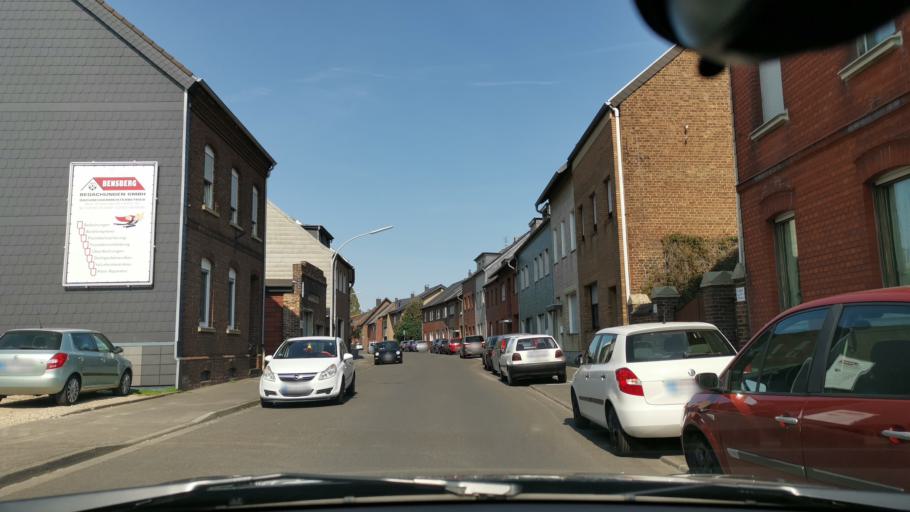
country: DE
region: North Rhine-Westphalia
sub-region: Regierungsbezirk Dusseldorf
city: Grevenbroich
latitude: 51.0745
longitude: 6.5675
